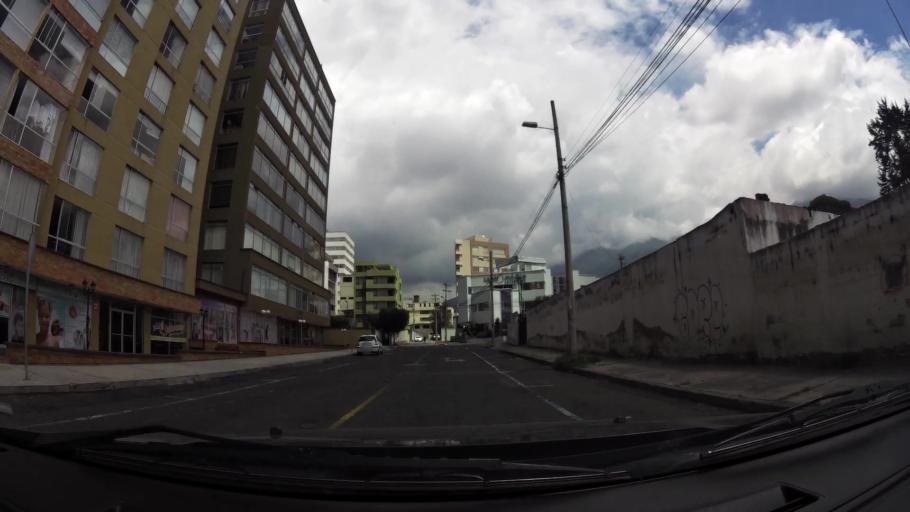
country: EC
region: Pichincha
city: Quito
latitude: -0.1816
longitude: -78.4884
